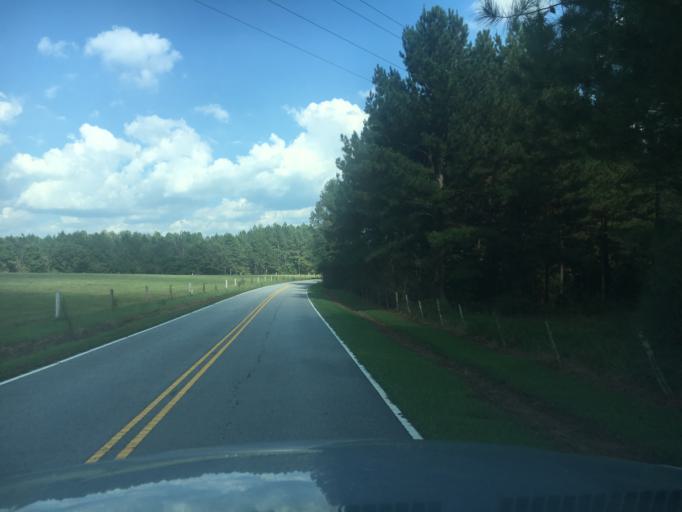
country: US
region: South Carolina
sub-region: Pickens County
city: Liberty
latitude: 34.7152
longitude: -82.6959
